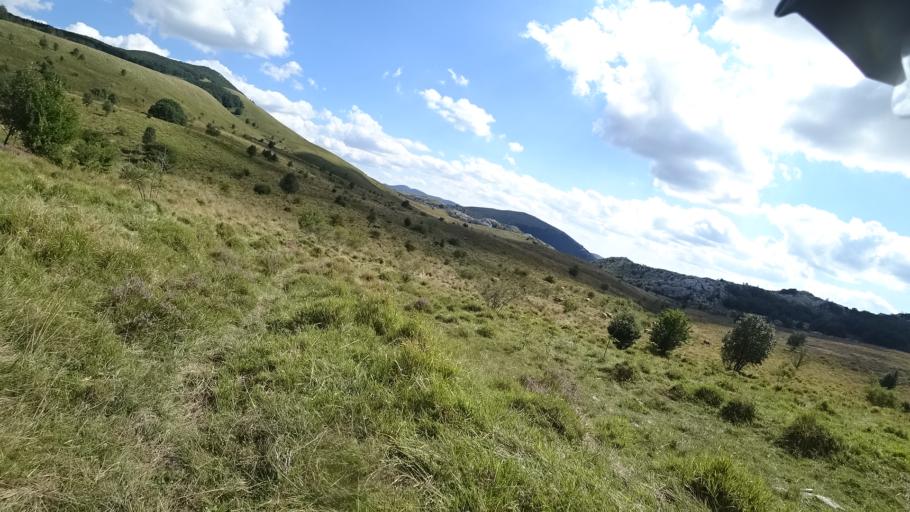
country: HR
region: Zadarska
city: Gracac
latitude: 44.4168
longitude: 16.0011
